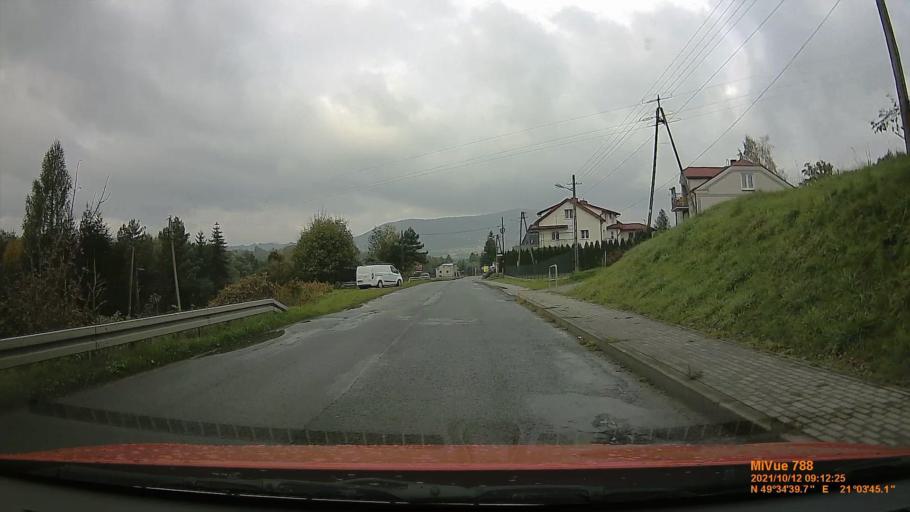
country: PL
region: Lesser Poland Voivodeship
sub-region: Powiat gorlicki
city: Ropa
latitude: 49.5777
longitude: 21.0624
